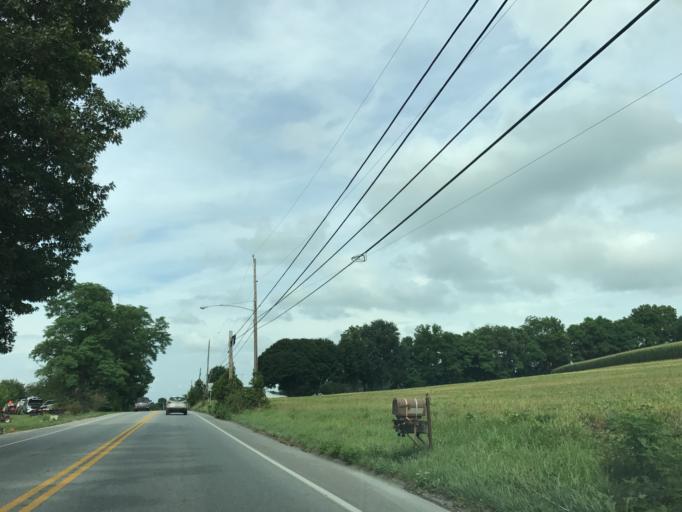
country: US
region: Pennsylvania
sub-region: York County
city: Parkville
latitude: 39.8296
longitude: -76.9277
